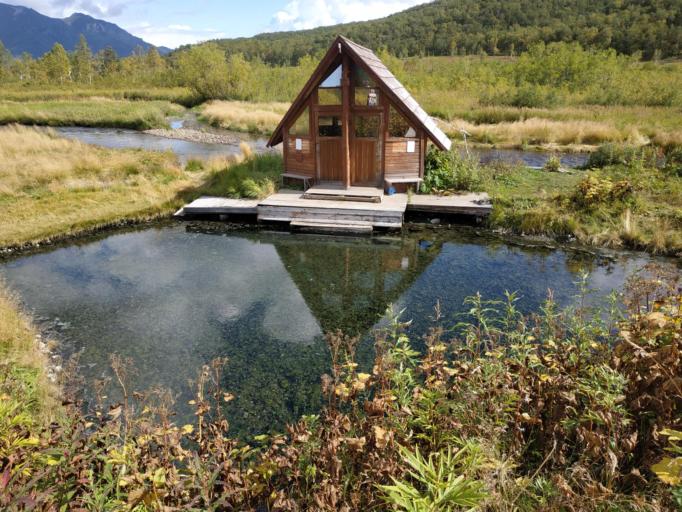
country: RU
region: Kamtsjatka
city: Petropavlovsk-Kamchatsky
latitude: 53.5057
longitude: 158.7633
